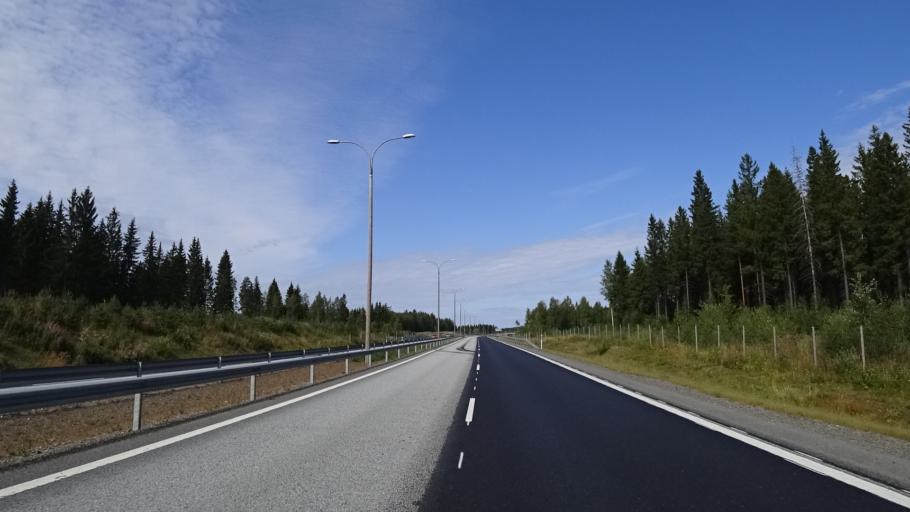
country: FI
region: North Karelia
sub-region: Joensuu
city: Joensuu
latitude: 62.5590
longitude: 29.8374
